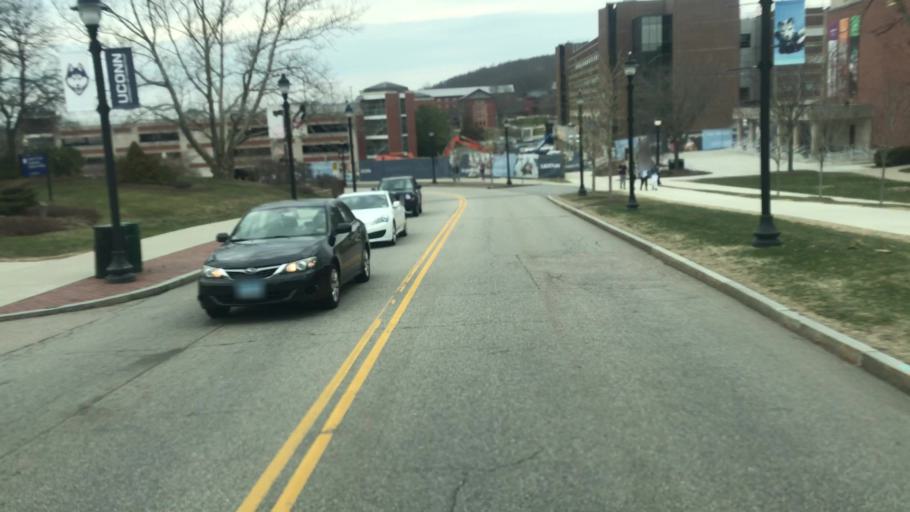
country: US
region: Connecticut
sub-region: Tolland County
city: Storrs
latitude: 41.8078
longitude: -72.2562
